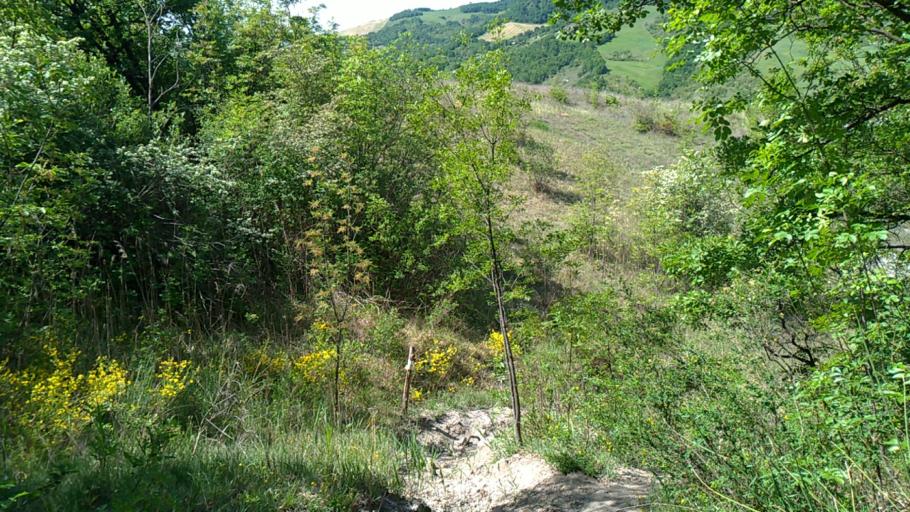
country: IT
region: Emilia-Romagna
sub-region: Provincia di Modena
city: Guiglia
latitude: 44.4121
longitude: 10.9276
